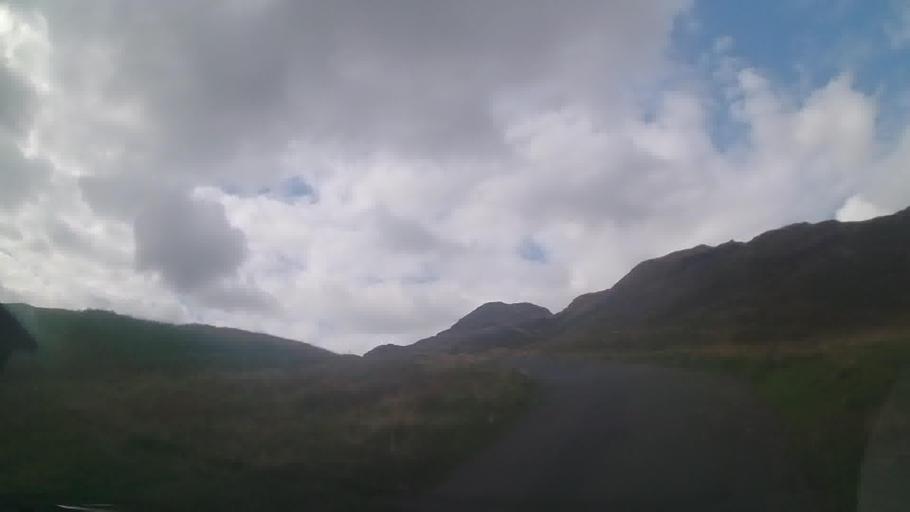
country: GB
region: England
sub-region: Cumbria
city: Keswick
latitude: 54.4032
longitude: -3.1789
